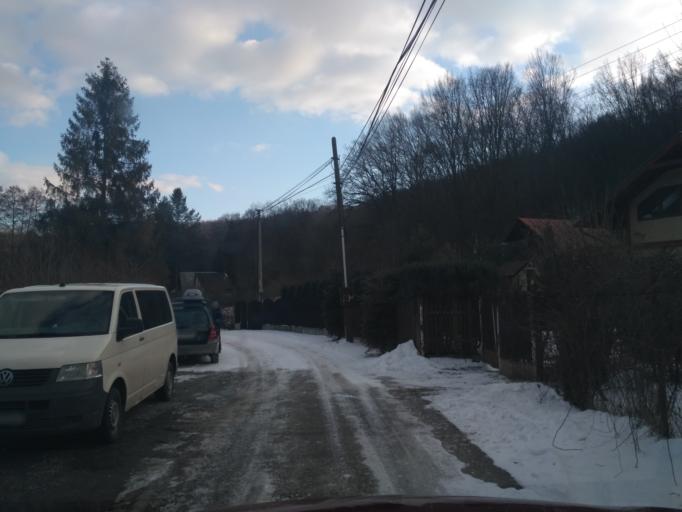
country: SK
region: Kosicky
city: Kosice
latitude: 48.7287
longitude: 21.1626
